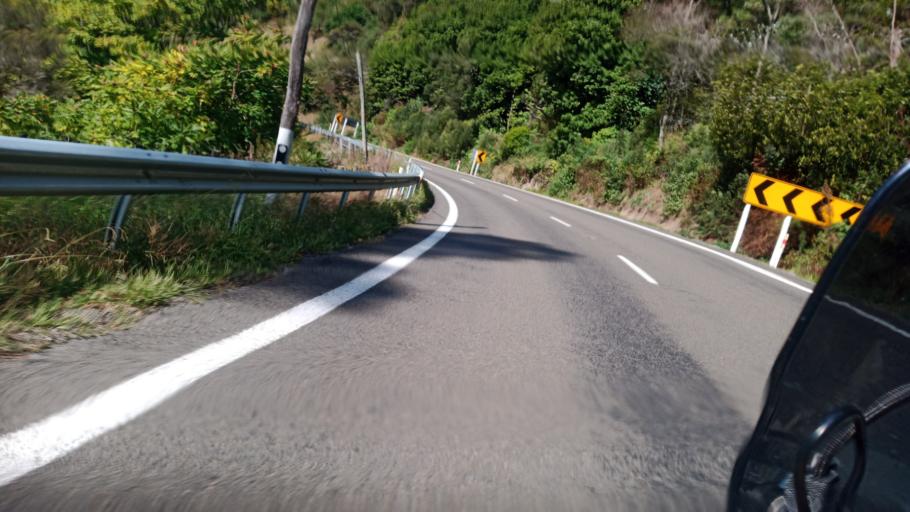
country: NZ
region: Gisborne
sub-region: Gisborne District
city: Gisborne
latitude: -38.4721
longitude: 177.6679
